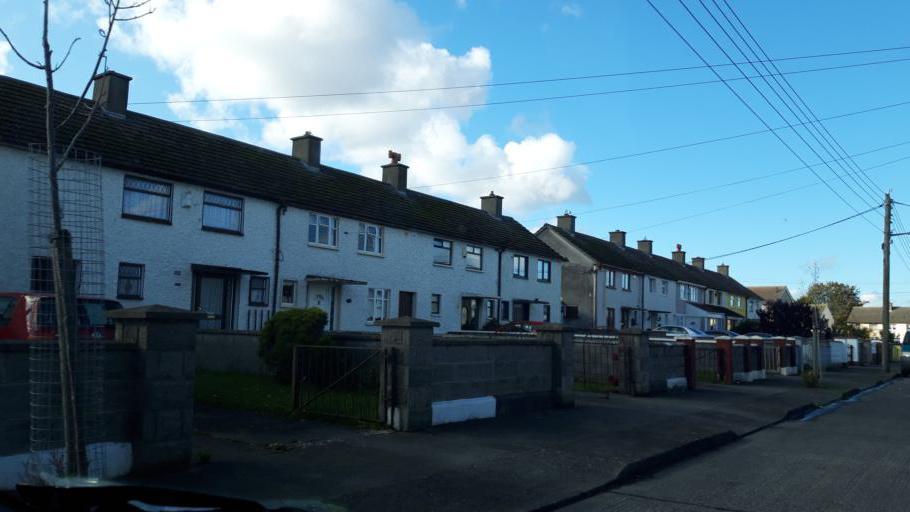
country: IE
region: Leinster
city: Raheny
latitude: 53.3857
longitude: -6.1852
